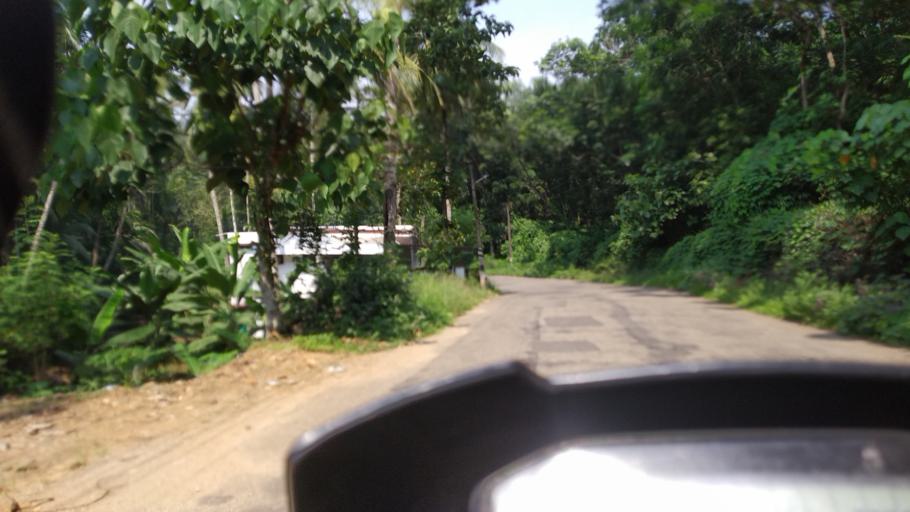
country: IN
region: Kerala
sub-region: Kottayam
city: Erattupetta
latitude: 9.6976
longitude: 76.8244
